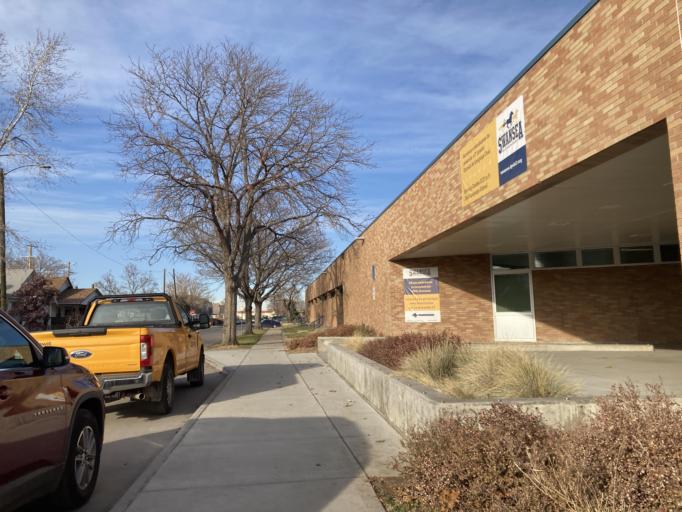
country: US
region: Colorado
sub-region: Adams County
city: Commerce City
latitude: 39.7811
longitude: -104.9570
